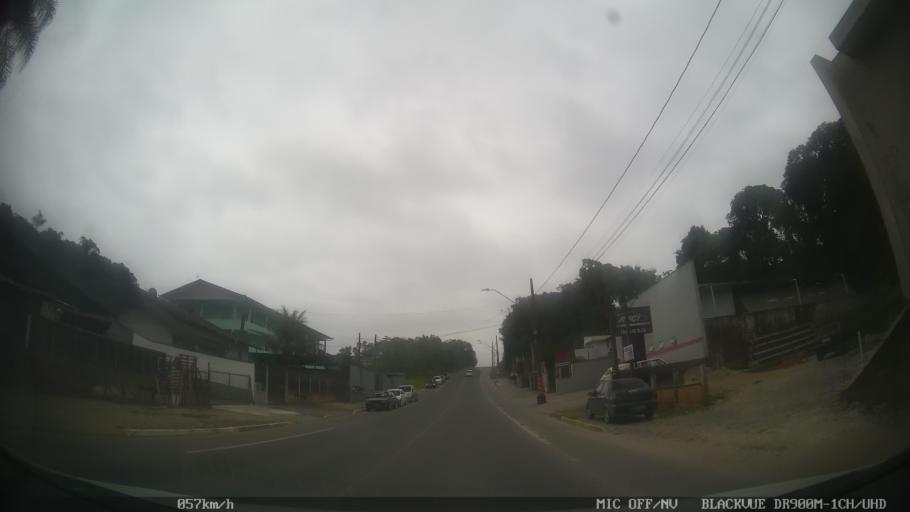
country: BR
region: Santa Catarina
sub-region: Joinville
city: Joinville
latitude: -26.3592
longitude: -48.8393
